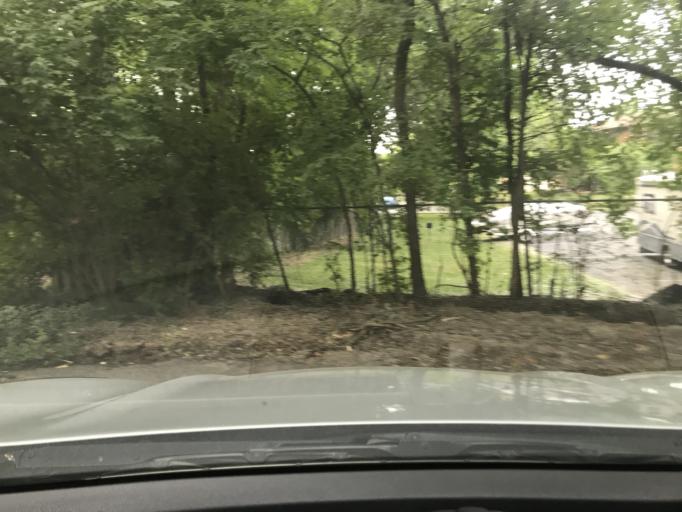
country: US
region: Tennessee
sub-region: Davidson County
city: Goodlettsville
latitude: 36.3097
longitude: -86.7084
